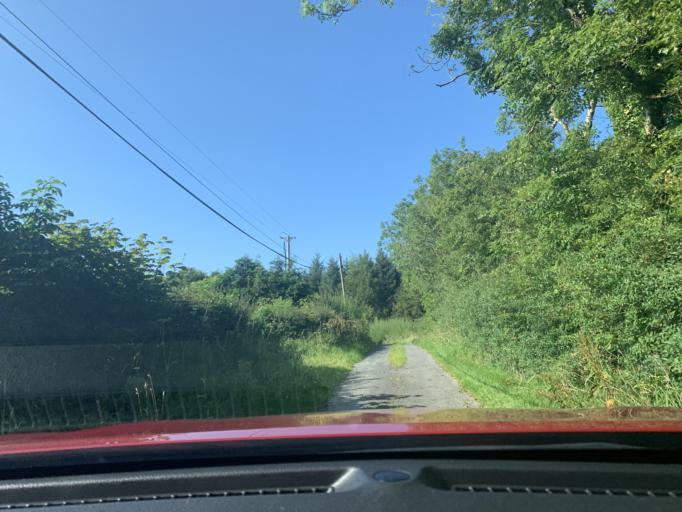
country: IE
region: Connaught
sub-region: Sligo
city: Tobercurry
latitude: 54.0598
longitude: -8.7936
